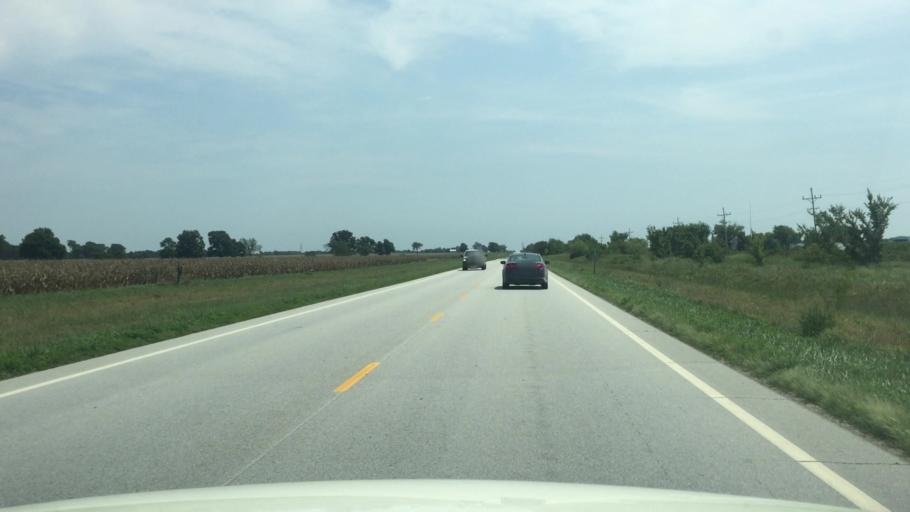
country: US
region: Kansas
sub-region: Cherokee County
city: Columbus
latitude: 37.1792
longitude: -94.9275
